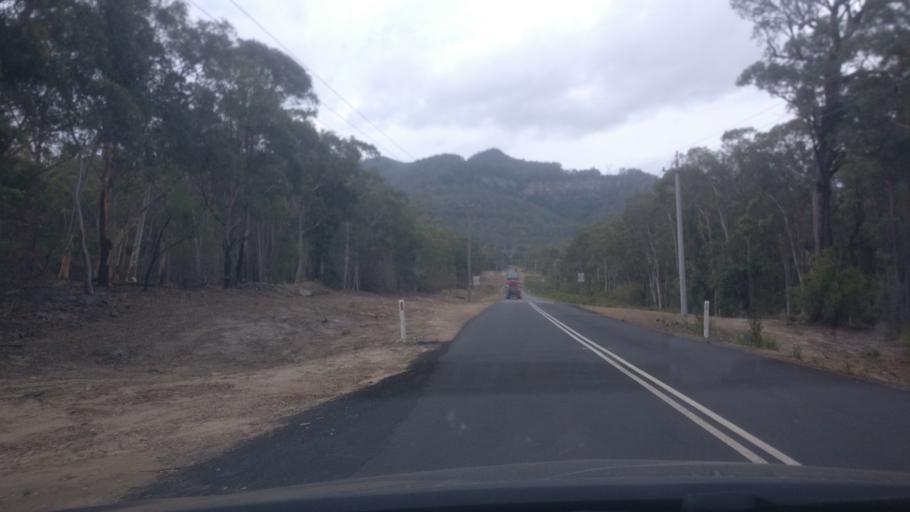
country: AU
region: New South Wales
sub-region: Shoalhaven Shire
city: Kangaroo Valley
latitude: -34.7341
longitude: 150.4795
